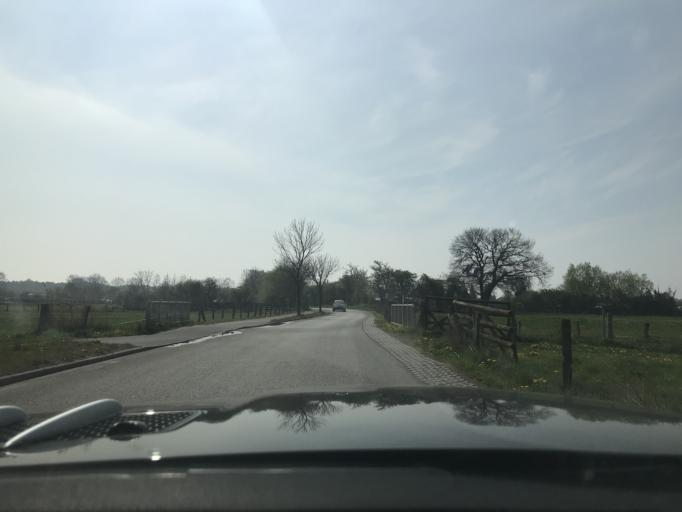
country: DE
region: Schleswig-Holstein
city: Gromitz
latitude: 54.1620
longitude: 10.9855
